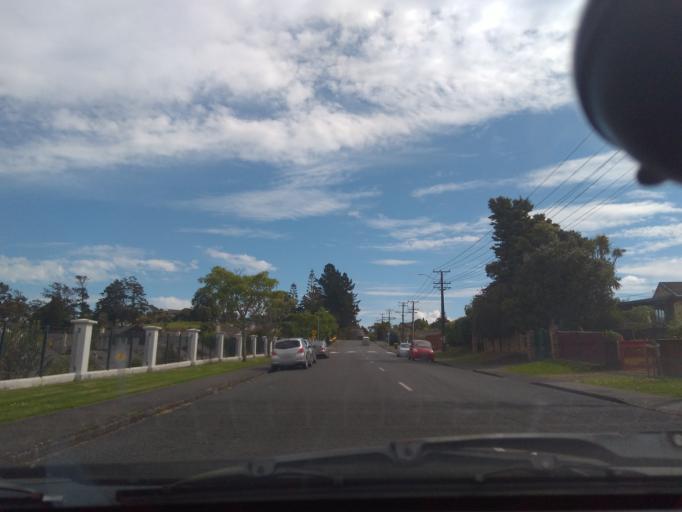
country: NZ
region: Auckland
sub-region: Auckland
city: Titirangi
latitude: -36.9349
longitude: 174.6721
